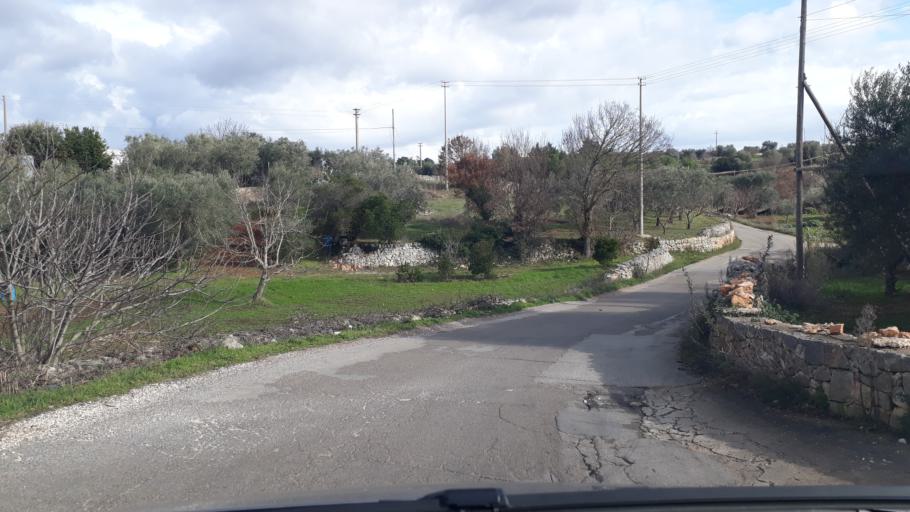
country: IT
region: Apulia
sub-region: Provincia di Brindisi
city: Cisternino
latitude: 40.7200
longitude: 17.4255
